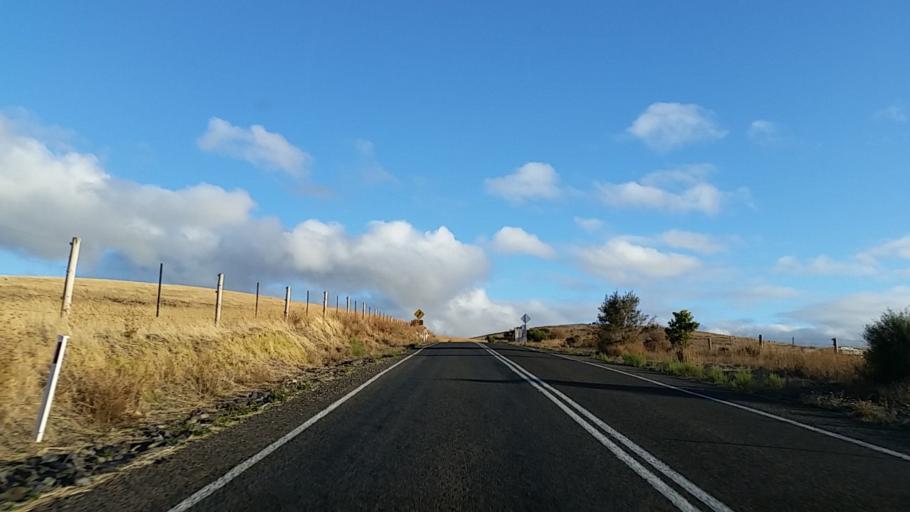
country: AU
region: South Australia
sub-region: Yankalilla
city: Normanville
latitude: -35.5354
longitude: 138.1944
